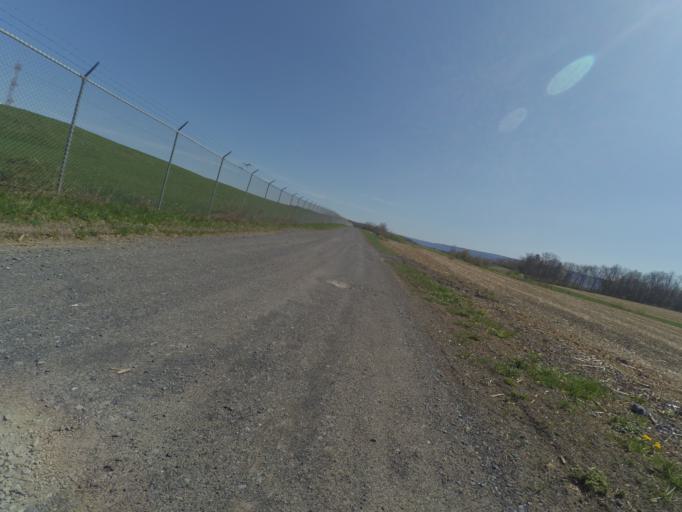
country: US
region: Pennsylvania
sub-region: Centre County
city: Houserville
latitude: 40.8526
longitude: -77.8401
